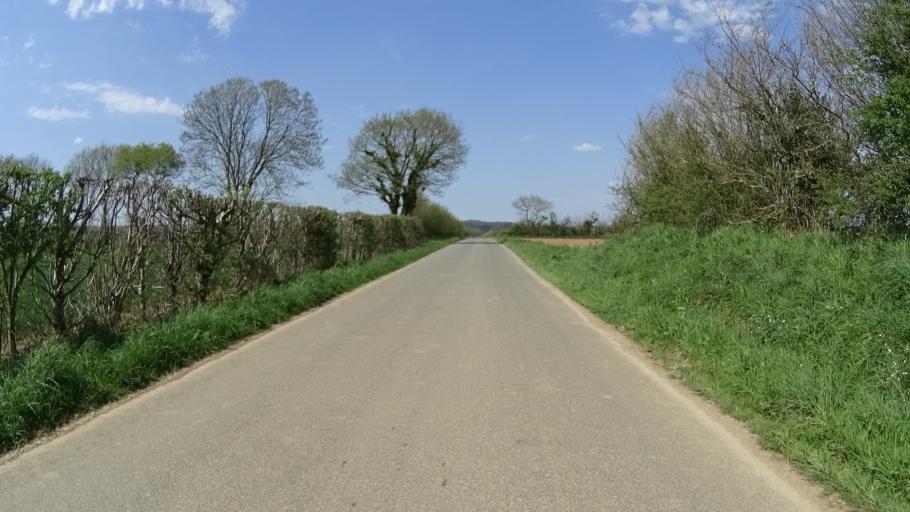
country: FR
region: Brittany
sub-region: Departement du Finistere
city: Sizun
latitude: 48.4211
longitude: -4.0878
